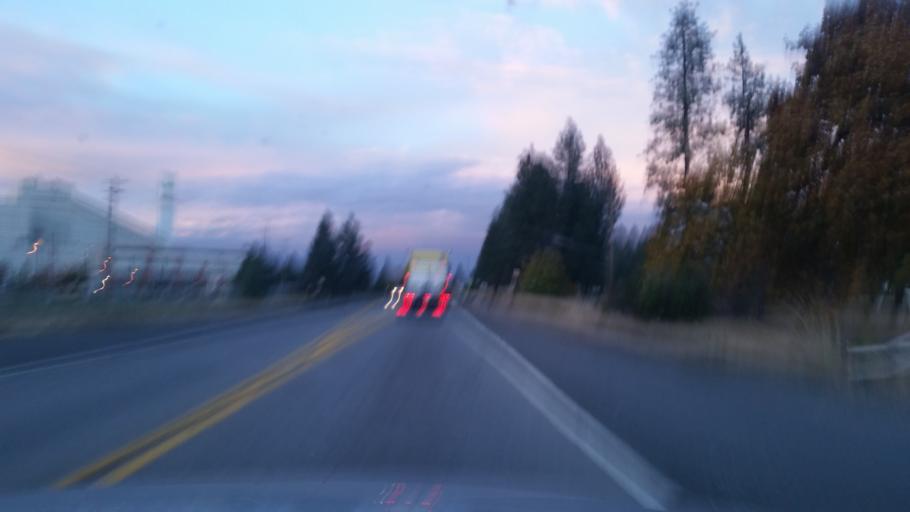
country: US
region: Washington
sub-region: Spokane County
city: Spokane
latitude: 47.6234
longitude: -117.5047
